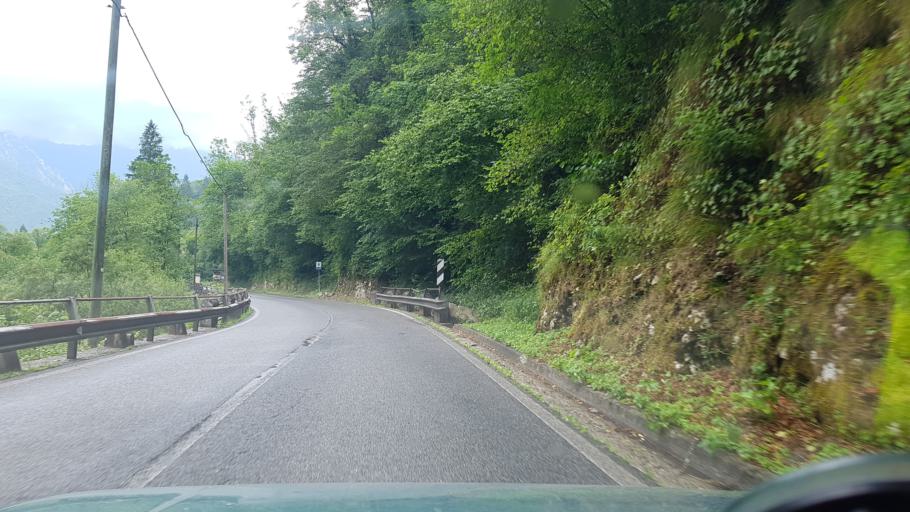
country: IT
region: Friuli Venezia Giulia
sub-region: Provincia di Udine
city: Lusevera
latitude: 46.2550
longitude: 13.2565
